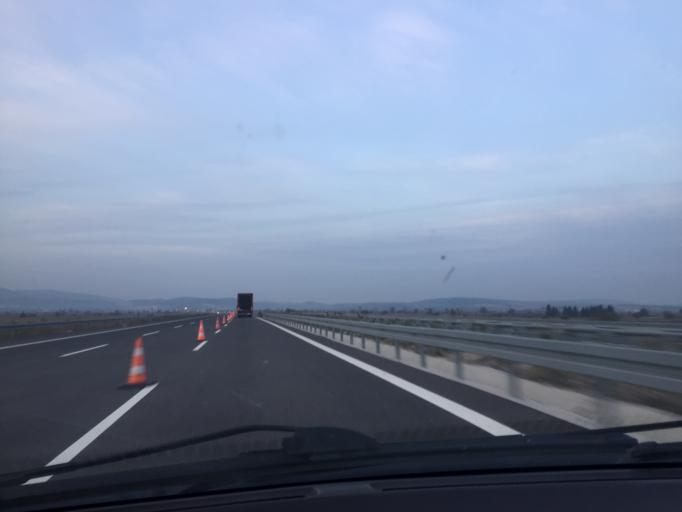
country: TR
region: Manisa
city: Halitpasa
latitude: 38.7393
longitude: 27.6579
